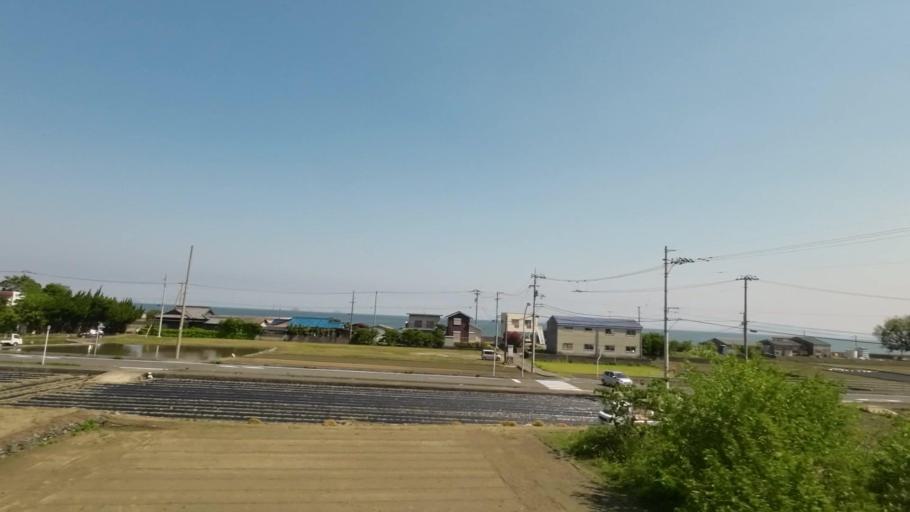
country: JP
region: Ehime
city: Kawanoecho
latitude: 33.9704
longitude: 133.4825
